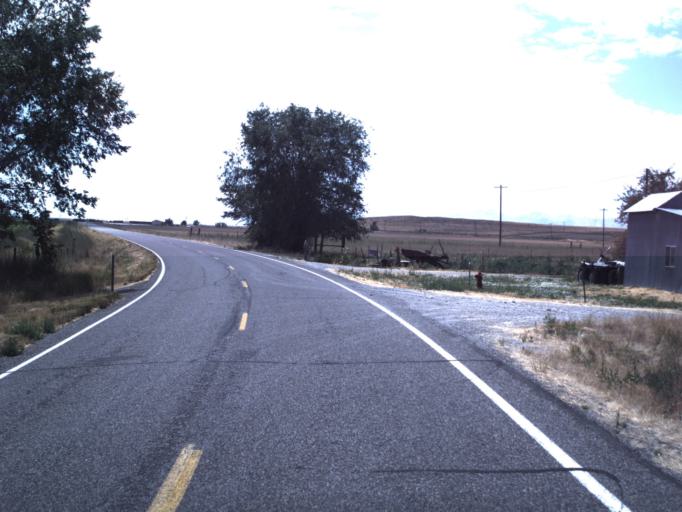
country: US
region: Utah
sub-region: Box Elder County
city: Tremonton
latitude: 41.6350
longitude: -112.3307
